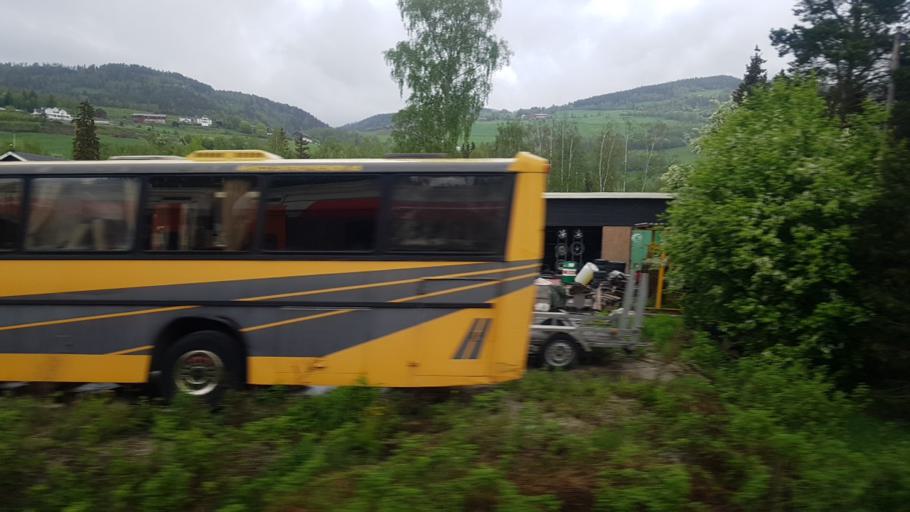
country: NO
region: Oppland
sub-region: Nord-Fron
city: Vinstra
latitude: 61.5826
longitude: 9.7596
